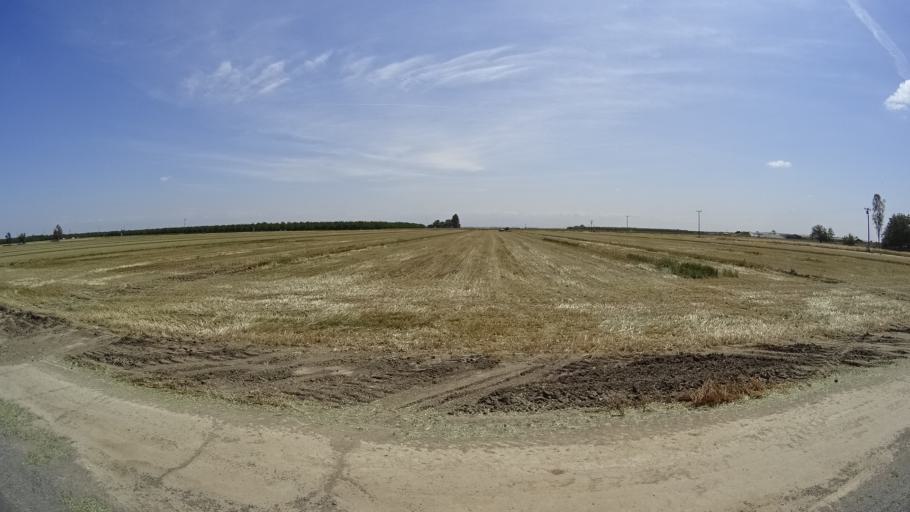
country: US
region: California
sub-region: Tulare County
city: Goshen
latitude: 36.3235
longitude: -119.4932
